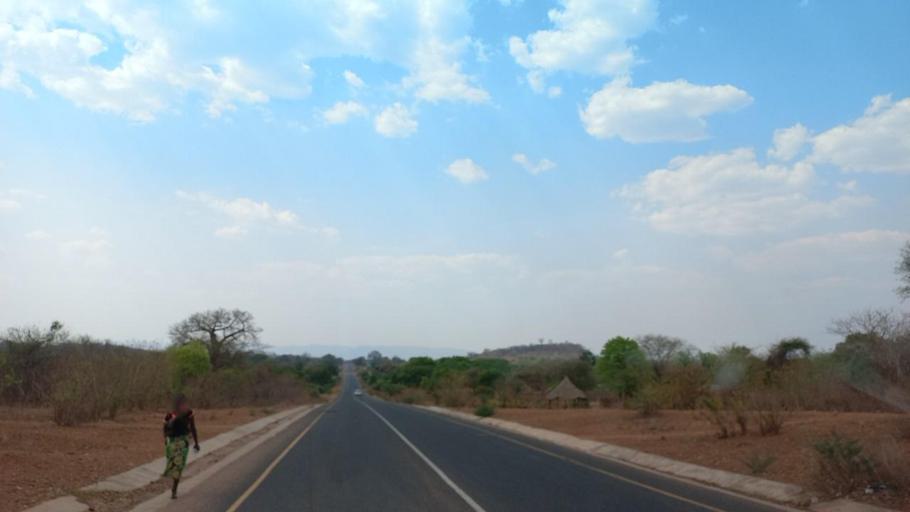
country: ZM
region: Lusaka
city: Luangwa
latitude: -15.1989
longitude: 30.2236
